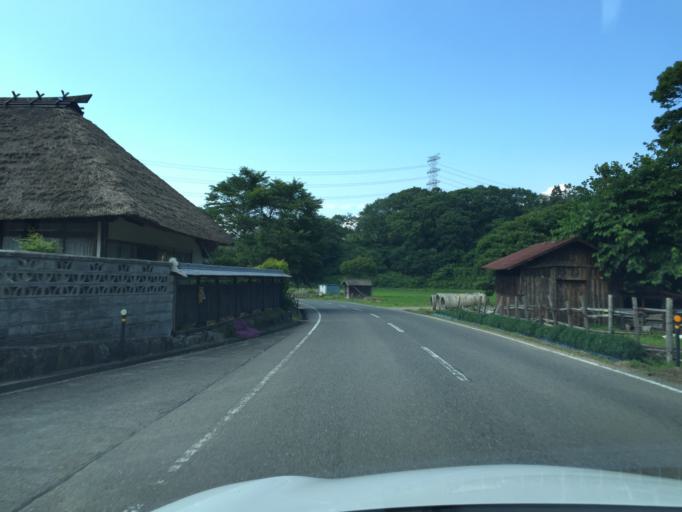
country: JP
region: Fukushima
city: Ishikawa
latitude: 37.1704
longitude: 140.6190
